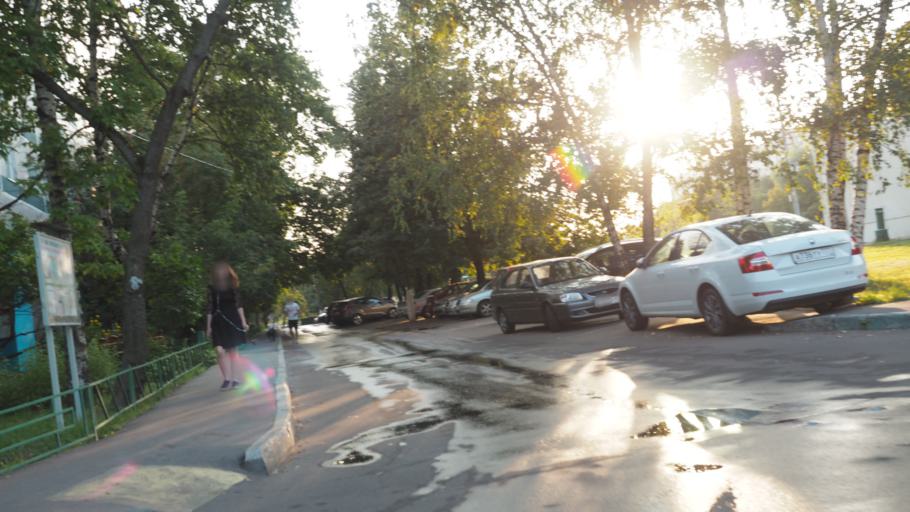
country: RU
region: Moscow
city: Orekhovo-Borisovo
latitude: 55.5997
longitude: 37.7170
